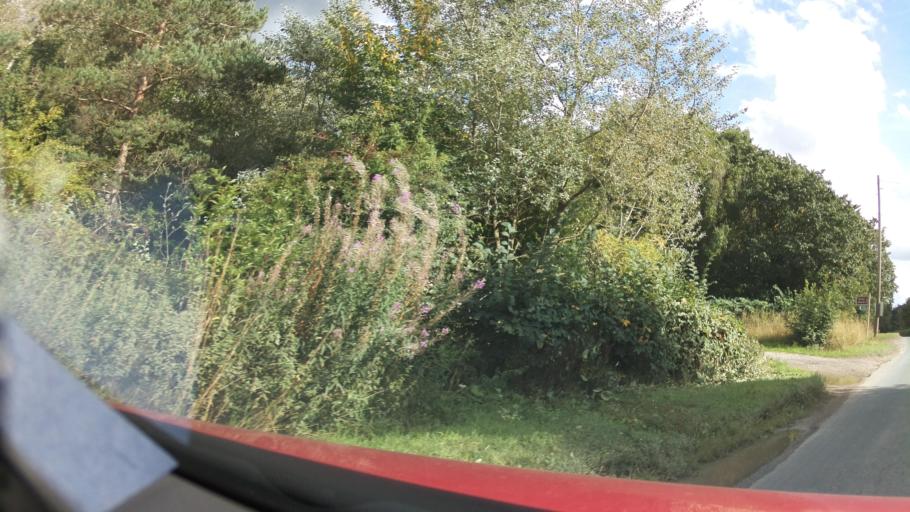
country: GB
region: England
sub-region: North Yorkshire
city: Bedale
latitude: 54.2358
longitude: -1.6745
